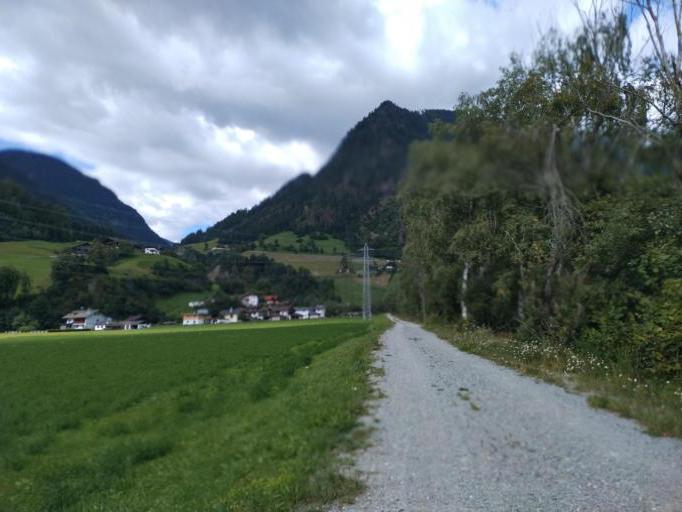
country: AT
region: Tyrol
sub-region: Politischer Bezirk Lienz
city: Hopfgarten in Defereggen
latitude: 46.9283
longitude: 12.5862
